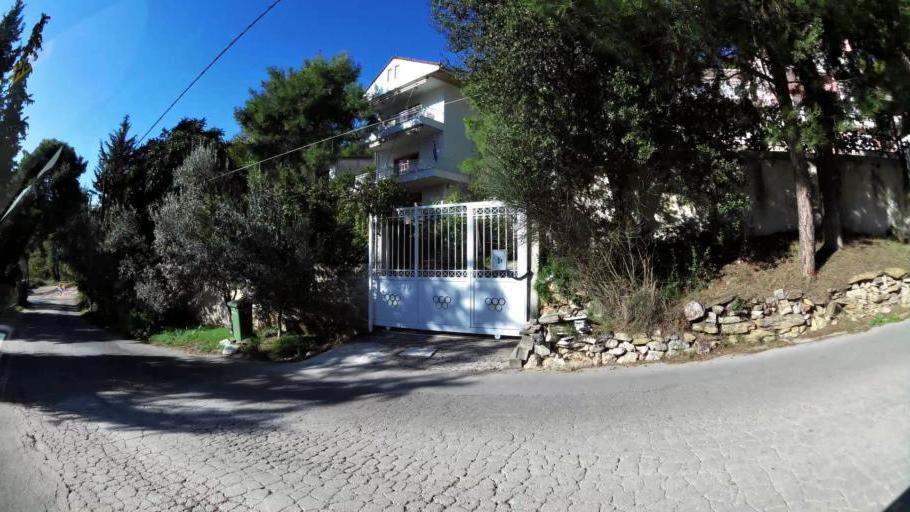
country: GR
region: Attica
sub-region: Nomarchia Anatolikis Attikis
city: Stamata
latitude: 38.1306
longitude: 23.8795
